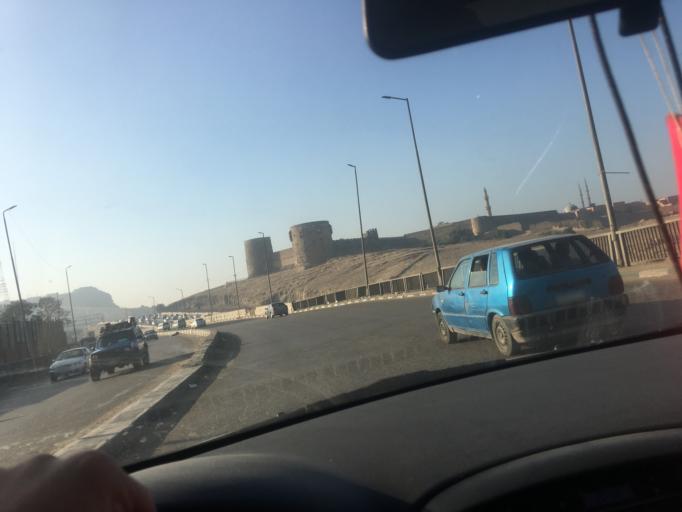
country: EG
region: Muhafazat al Qahirah
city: Cairo
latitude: 30.0339
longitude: 31.2676
